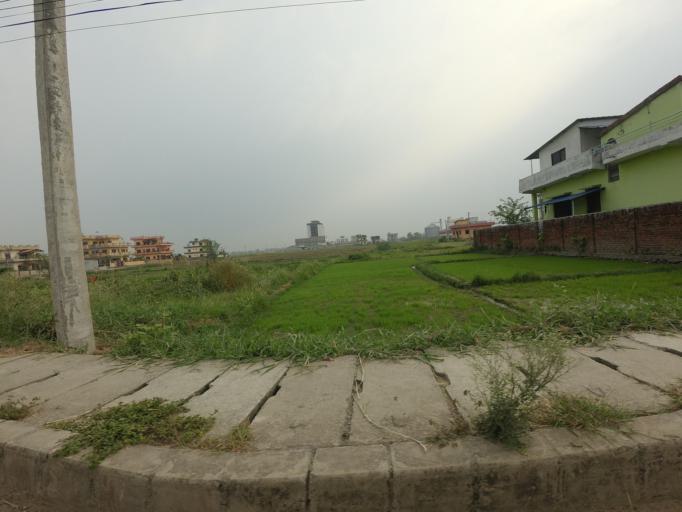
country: NP
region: Western Region
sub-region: Lumbini Zone
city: Bhairahawa
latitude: 27.5255
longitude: 83.4514
